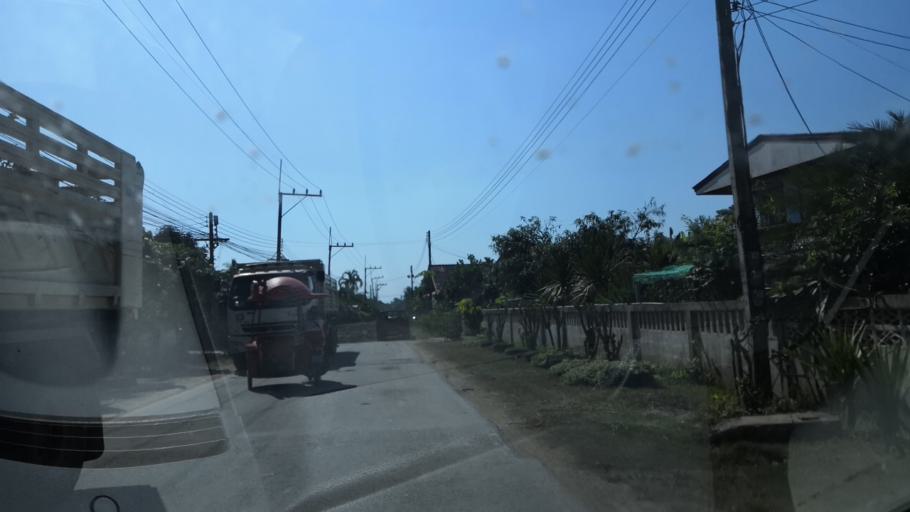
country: TH
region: Chiang Rai
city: Wiang Chai
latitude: 19.8915
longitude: 99.9513
